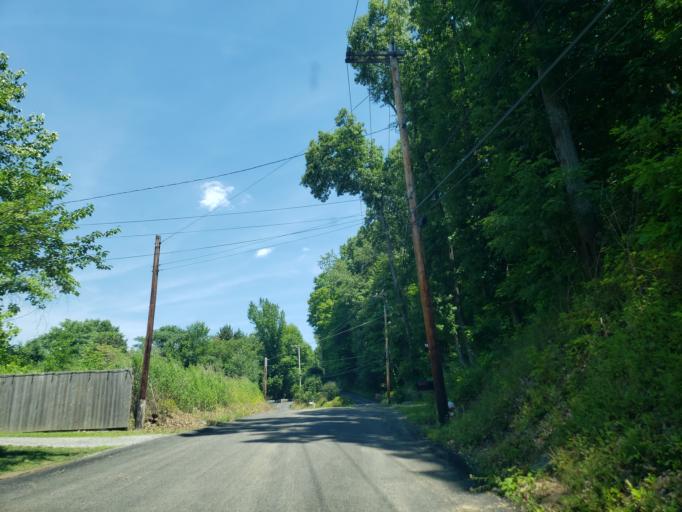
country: US
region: Pennsylvania
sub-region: Allegheny County
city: Emsworth
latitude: 40.5232
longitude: -80.0927
